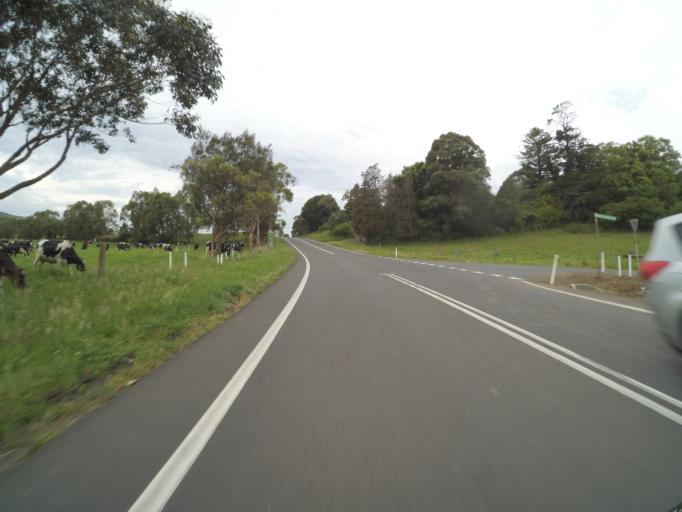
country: AU
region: New South Wales
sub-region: Kiama
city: Jamberoo
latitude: -34.6524
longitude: 150.7976
